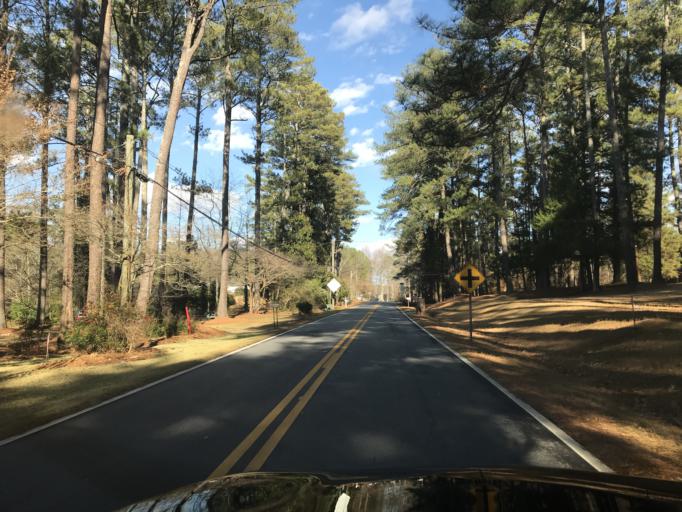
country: US
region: Georgia
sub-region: Cobb County
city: Mableton
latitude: 33.7114
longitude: -84.5563
